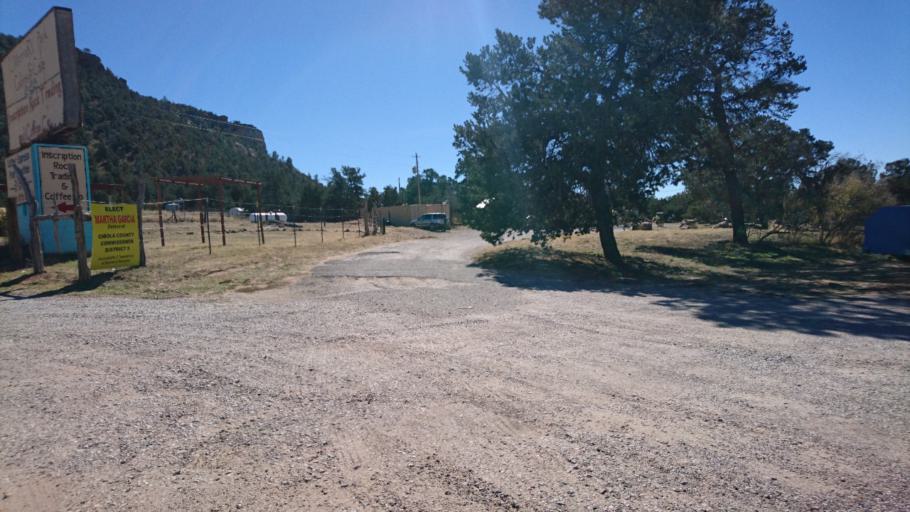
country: US
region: New Mexico
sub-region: McKinley County
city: Thoreau
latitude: 35.0443
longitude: -108.3196
